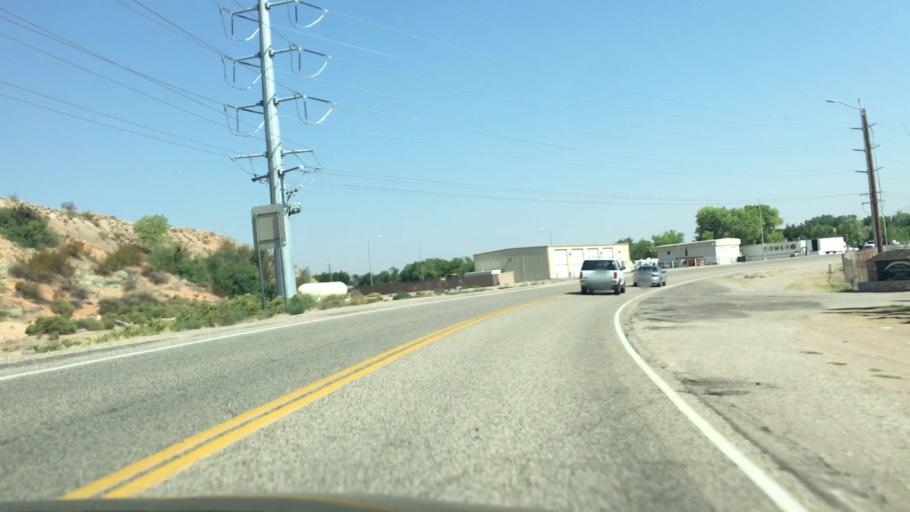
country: US
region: Arizona
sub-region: Mohave County
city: Beaver Dam
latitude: 36.8983
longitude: -113.9345
